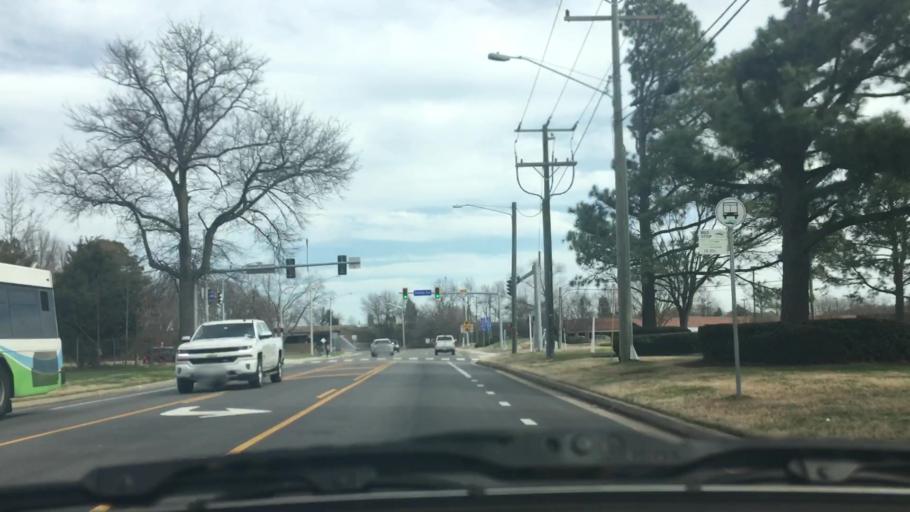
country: US
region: Virginia
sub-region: City of Norfolk
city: Norfolk
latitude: 36.8809
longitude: -76.2182
